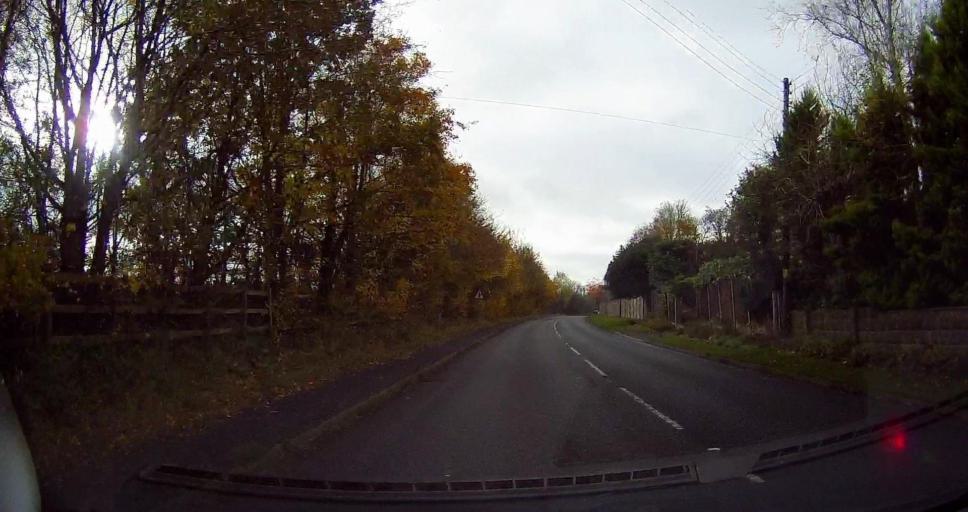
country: GB
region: England
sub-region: Kent
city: Meopham
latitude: 51.3329
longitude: 0.3435
